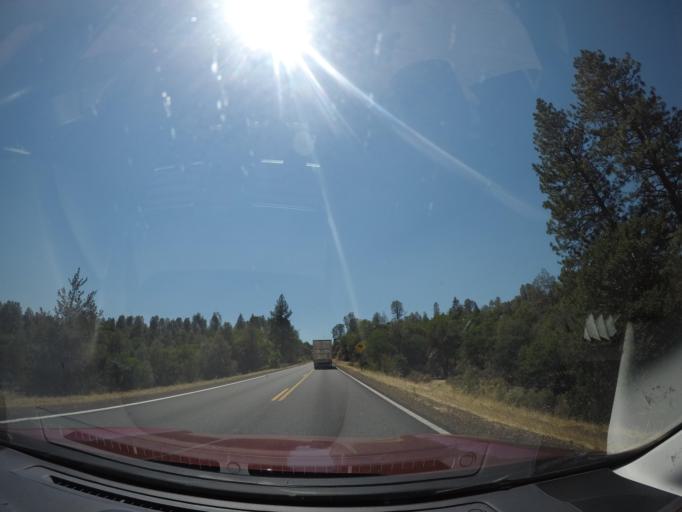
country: US
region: California
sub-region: Shasta County
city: Burney
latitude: 40.9972
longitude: -121.4580
